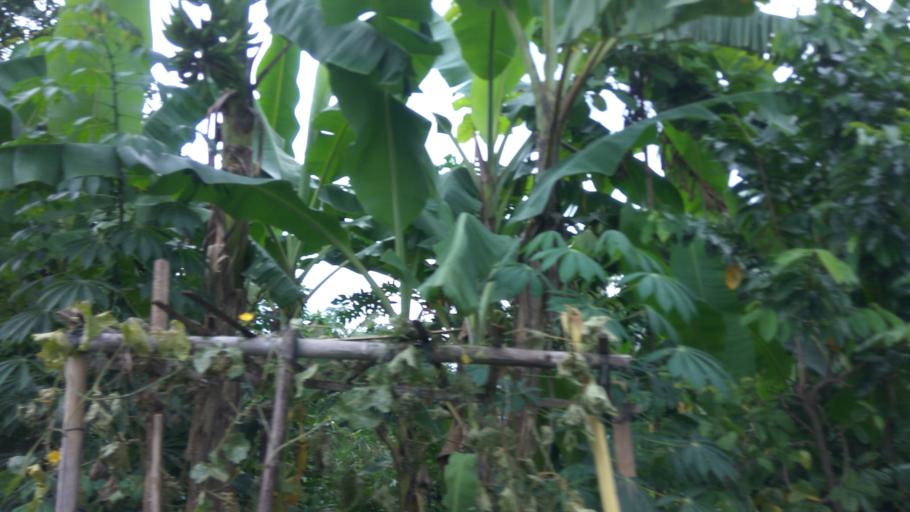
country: ID
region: Daerah Istimewa Yogyakarta
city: Depok
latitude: -7.7391
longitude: 110.4077
